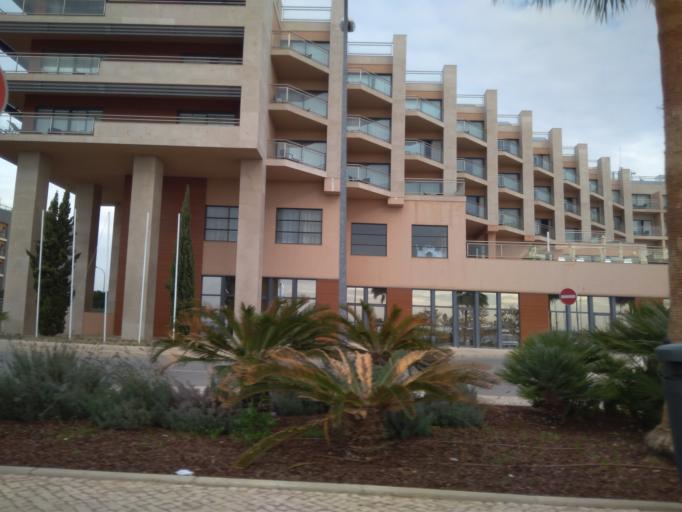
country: PT
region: Faro
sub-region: Olhao
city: Olhao
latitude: 37.0236
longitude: -7.8477
